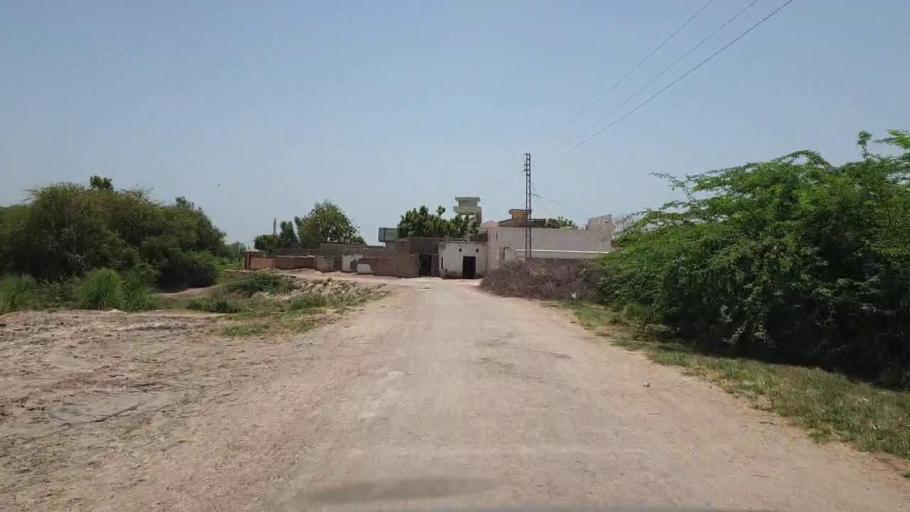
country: PK
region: Sindh
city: Sakrand
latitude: 26.1064
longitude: 68.3922
